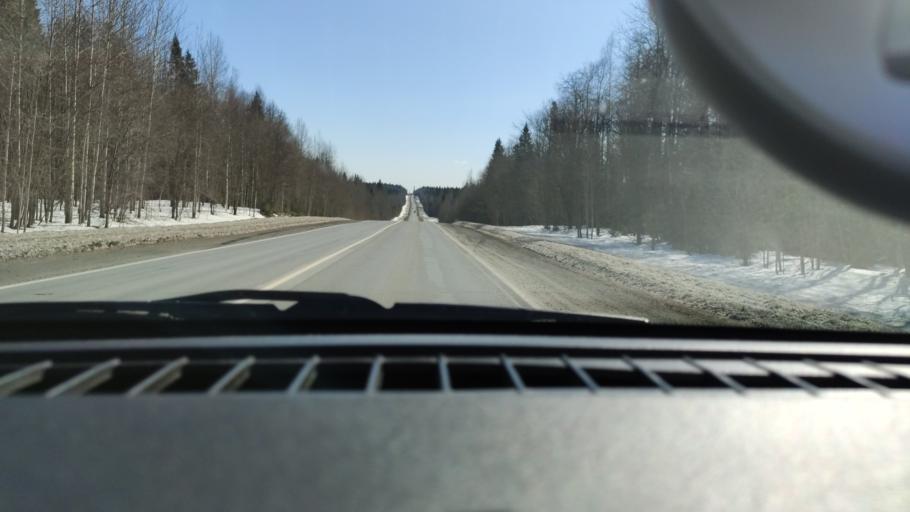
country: RU
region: Perm
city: Perm
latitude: 58.1688
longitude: 56.2367
